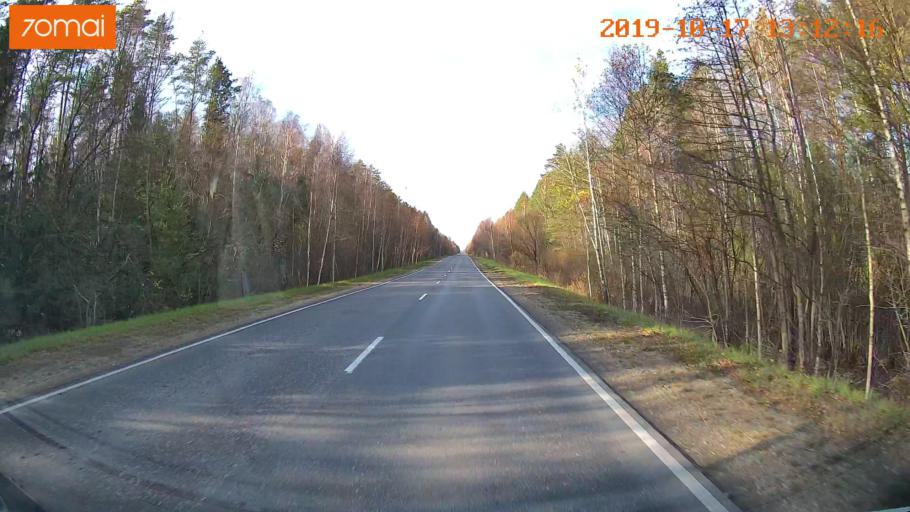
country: RU
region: Rjazan
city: Gus'-Zheleznyy
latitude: 55.0348
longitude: 41.2168
